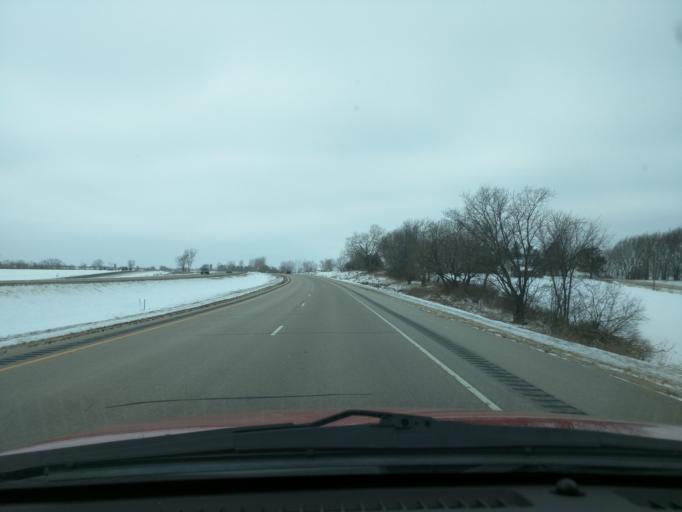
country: US
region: Wisconsin
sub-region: Trempealeau County
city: Trempealeau
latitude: 43.9258
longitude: -91.4818
